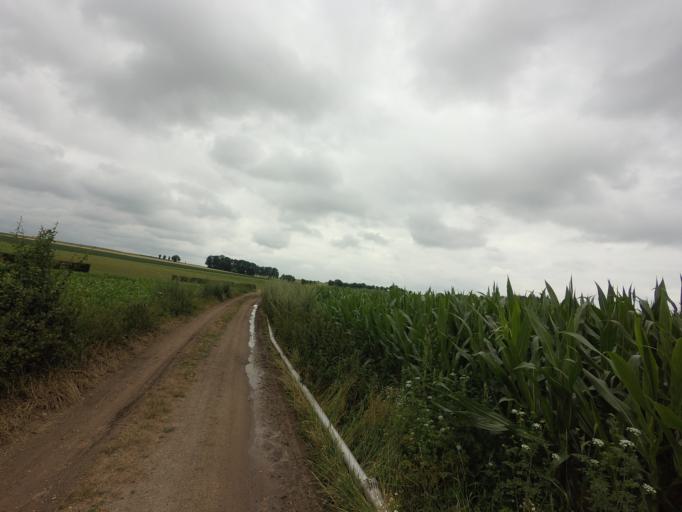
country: NL
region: Limburg
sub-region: Eijsden-Margraten
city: Margraten
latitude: 50.8097
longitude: 5.8185
